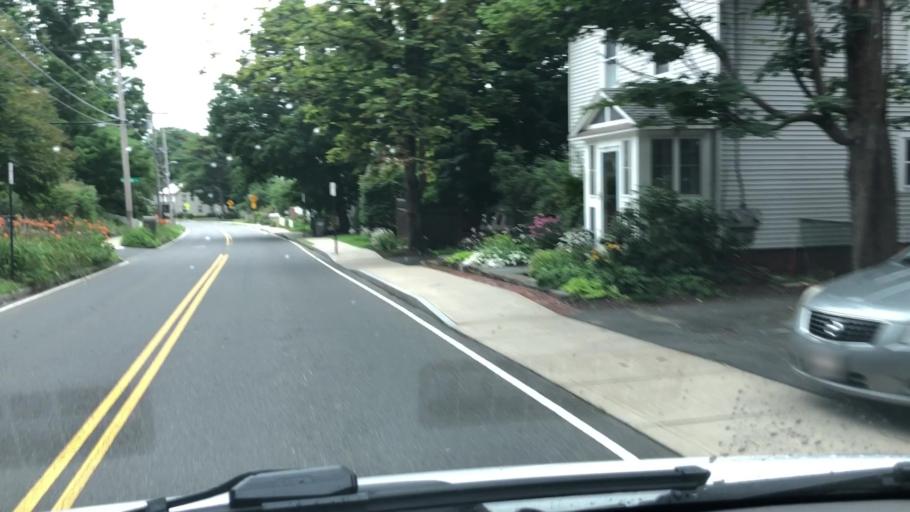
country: US
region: Massachusetts
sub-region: Hampshire County
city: Northampton
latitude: 42.3260
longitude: -72.6311
